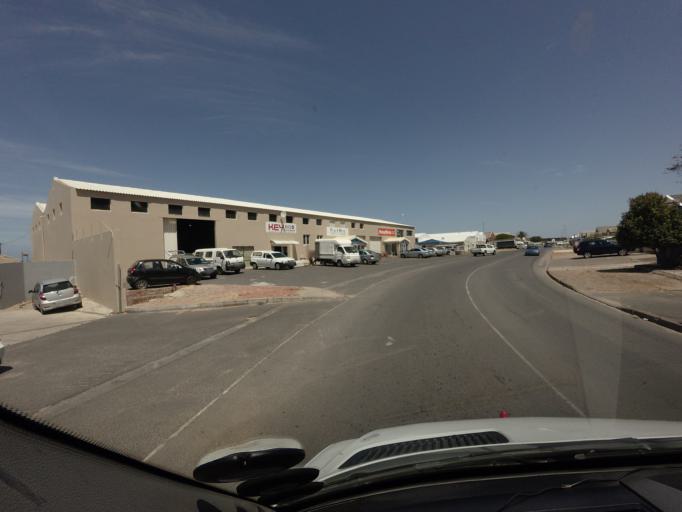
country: ZA
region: Western Cape
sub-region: Overberg District Municipality
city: Hermanus
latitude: -34.4214
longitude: 19.2241
